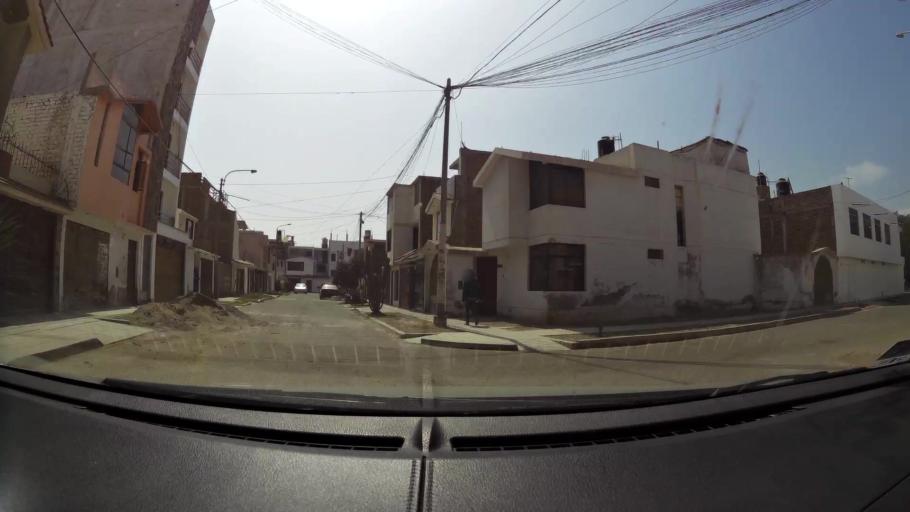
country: PE
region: La Libertad
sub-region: Provincia de Trujillo
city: Buenos Aires
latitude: -8.1348
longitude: -79.0518
